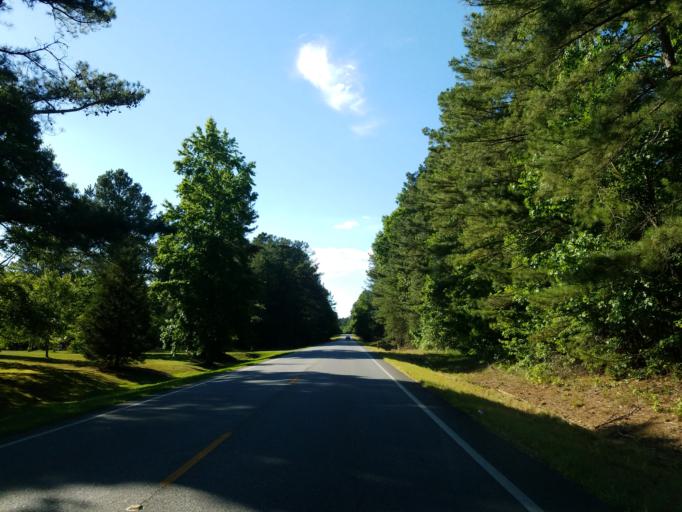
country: US
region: Georgia
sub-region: Gordon County
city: Calhoun
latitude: 34.6013
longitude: -85.0365
